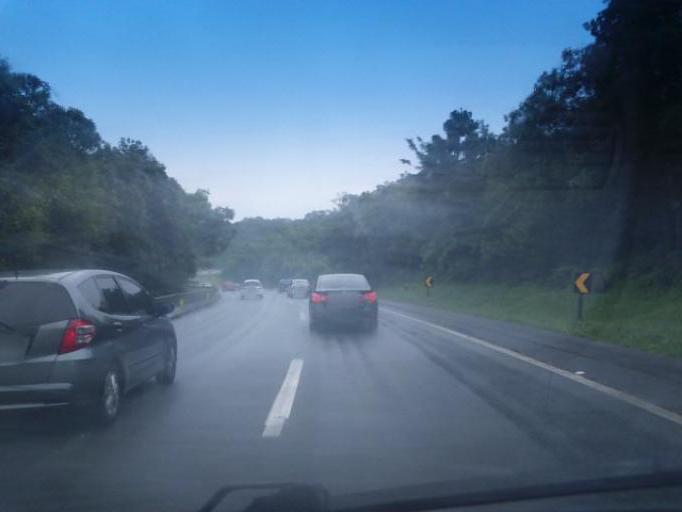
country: BR
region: Parana
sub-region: Sao Jose Dos Pinhais
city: Sao Jose dos Pinhais
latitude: -25.8436
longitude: -49.0145
